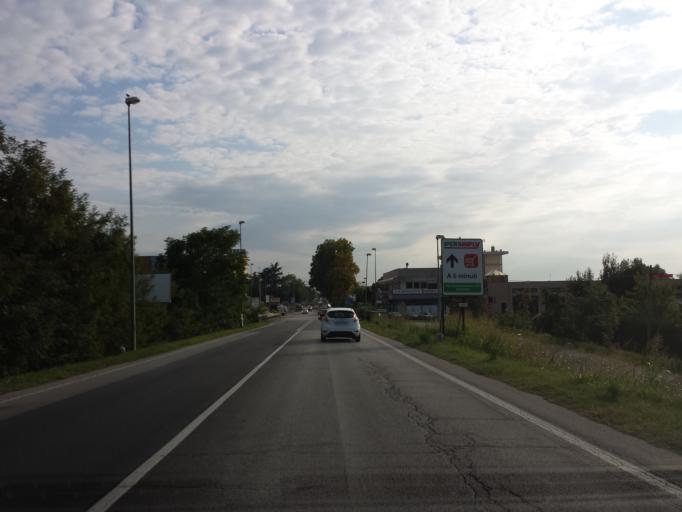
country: IT
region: Veneto
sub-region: Provincia di Rovigo
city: Rovigo
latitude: 45.0538
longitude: 11.7889
